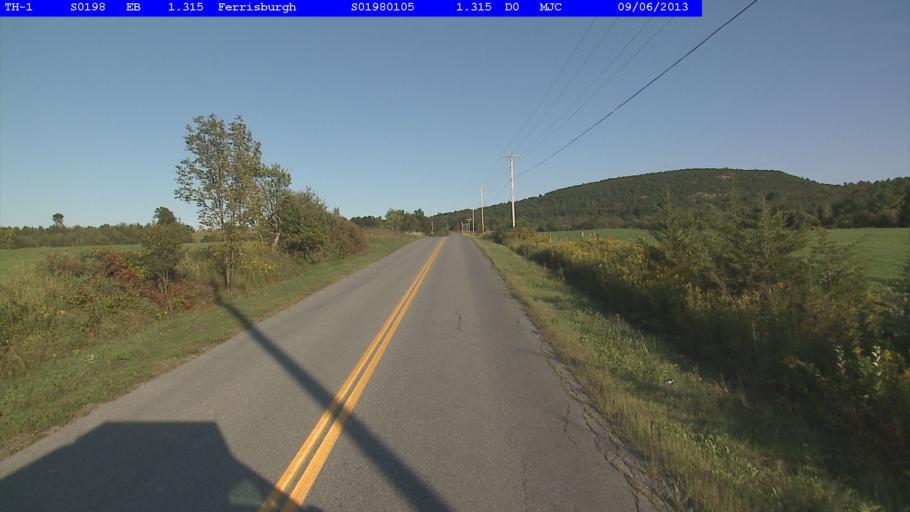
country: US
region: Vermont
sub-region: Addison County
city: Vergennes
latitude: 44.2566
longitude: -73.2026
